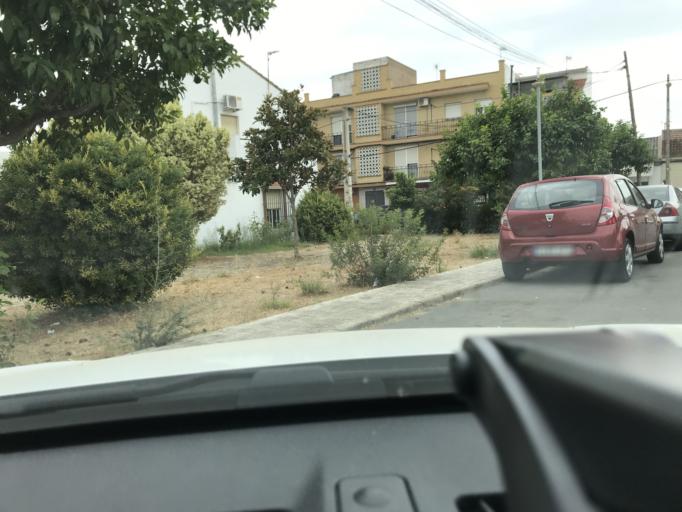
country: ES
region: Andalusia
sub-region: Provincia de Sevilla
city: Villanueva del Rio y Minas
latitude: 37.6490
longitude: -5.7108
